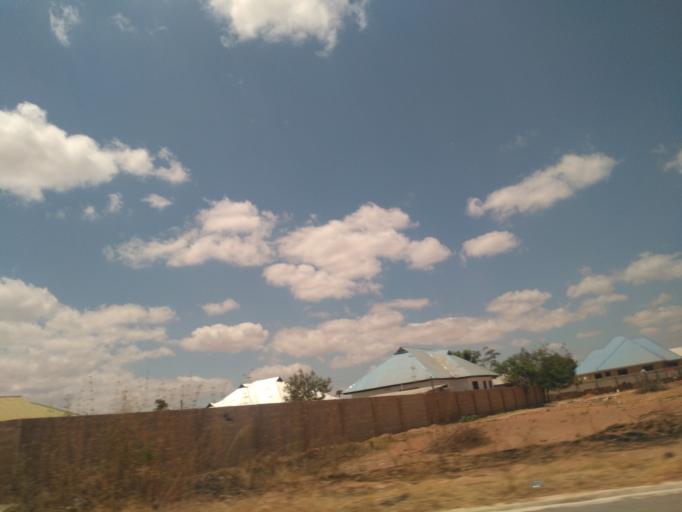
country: TZ
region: Dodoma
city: Kisasa
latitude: -6.1726
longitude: 35.8000
